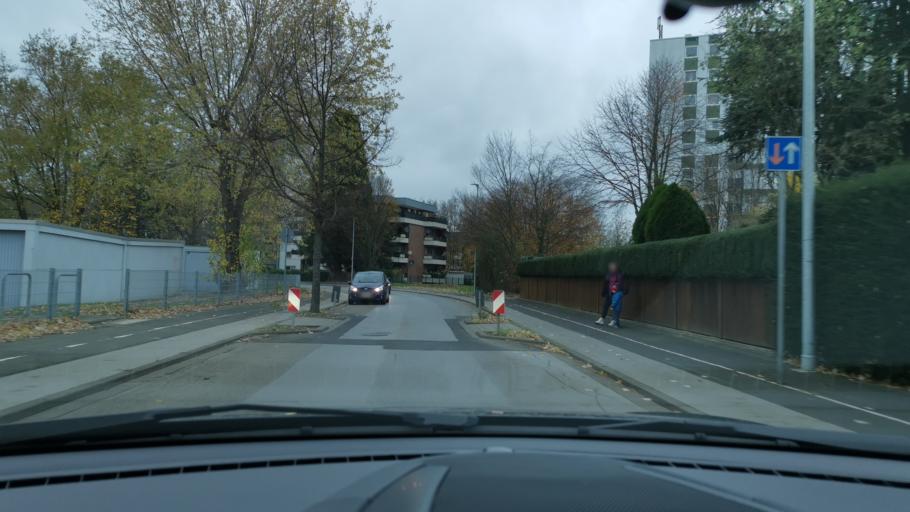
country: DE
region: North Rhine-Westphalia
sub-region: Regierungsbezirk Dusseldorf
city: Grevenbroich
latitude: 51.0775
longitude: 6.6003
